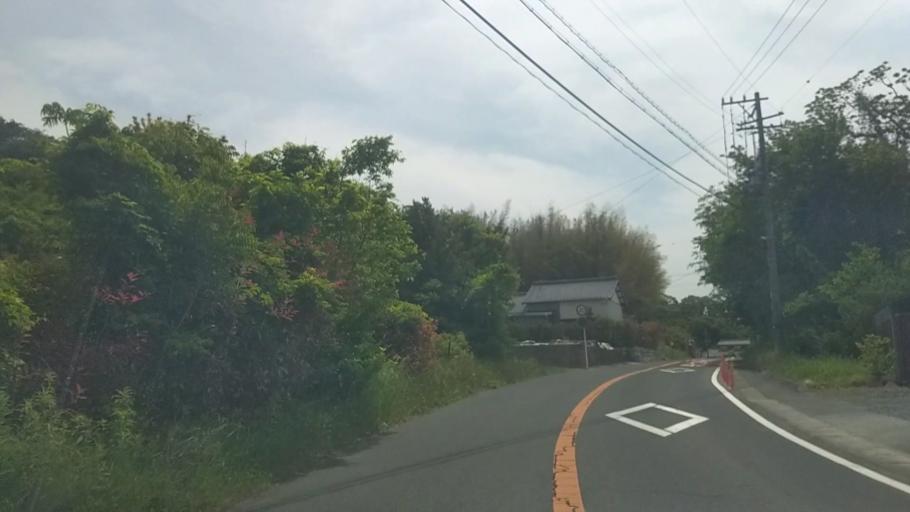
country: JP
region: Shizuoka
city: Kosai-shi
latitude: 34.7450
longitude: 137.5350
